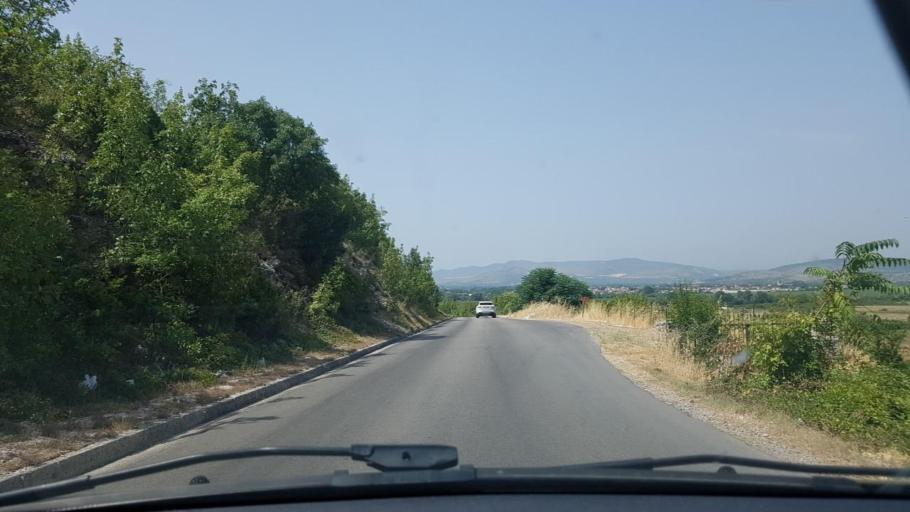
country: HR
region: Dubrovacko-Neretvanska
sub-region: Grad Dubrovnik
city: Metkovic
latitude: 43.0394
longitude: 17.7123
